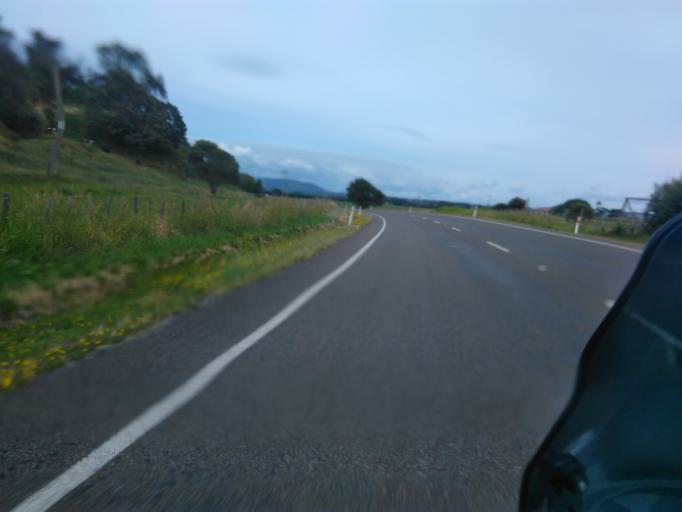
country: NZ
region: Bay of Plenty
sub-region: Opotiki District
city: Opotiki
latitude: -37.9919
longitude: 177.3060
